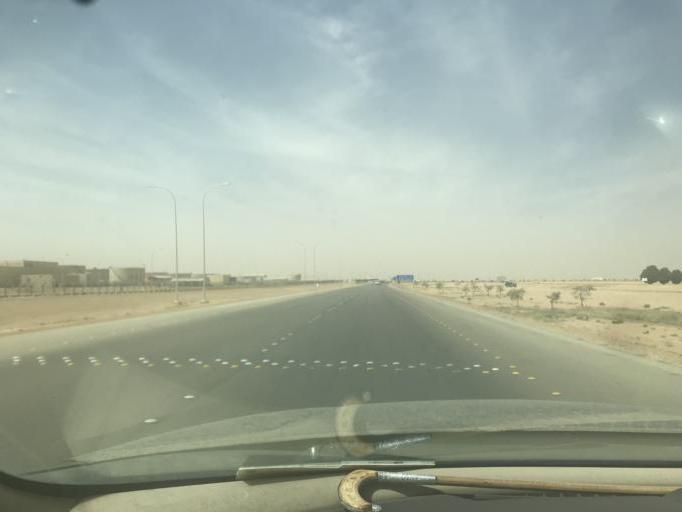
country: SA
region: Ar Riyad
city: Riyadh
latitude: 24.9793
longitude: 46.6853
